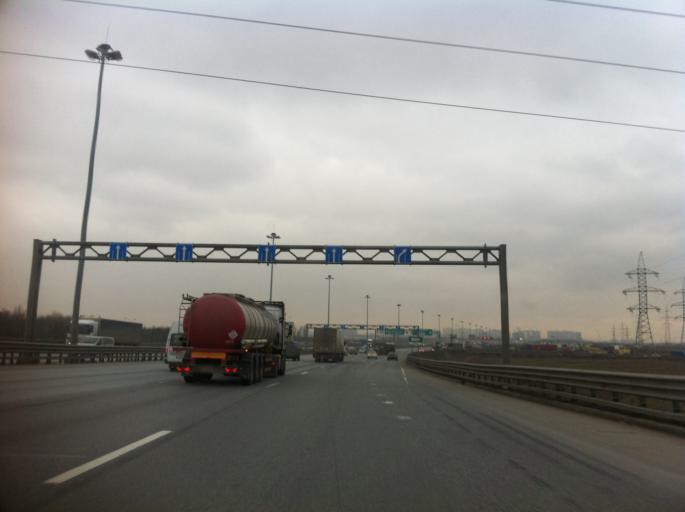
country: RU
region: St.-Petersburg
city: Obukhovo
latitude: 59.8261
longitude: 30.4352
